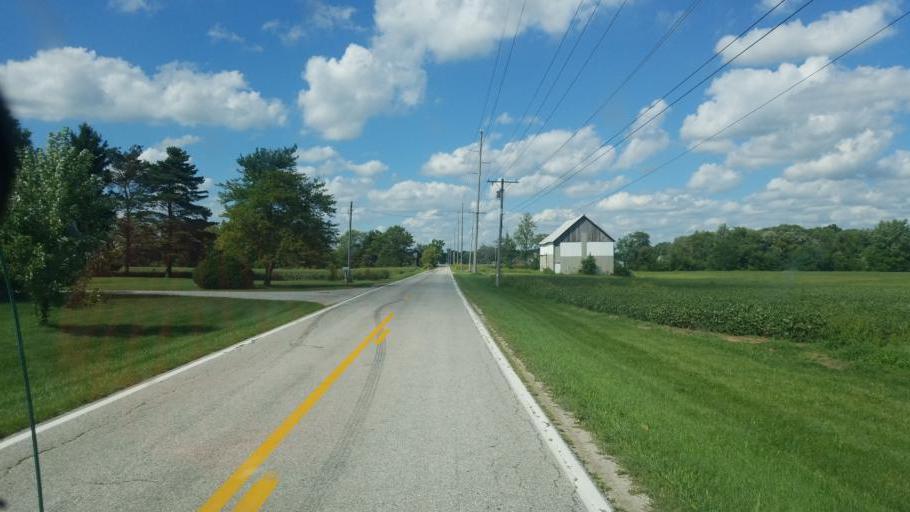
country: US
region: Ohio
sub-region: Delaware County
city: Delaware
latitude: 40.3120
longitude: -83.1998
